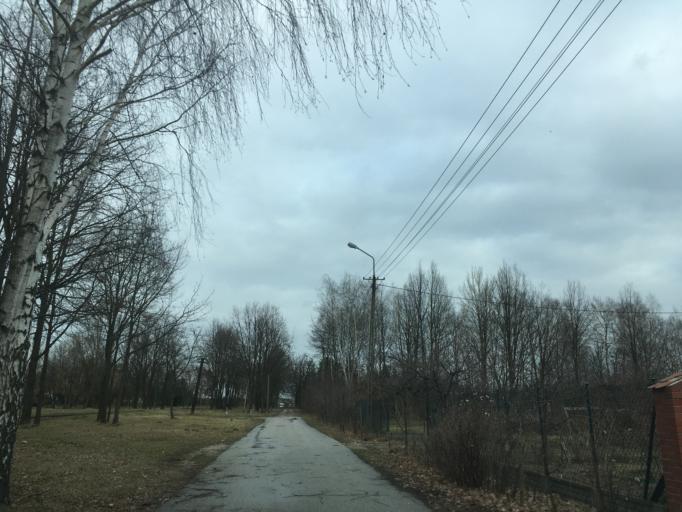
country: PL
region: Masovian Voivodeship
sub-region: Powiat piaseczynski
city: Lesznowola
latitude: 52.0358
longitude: 20.9613
